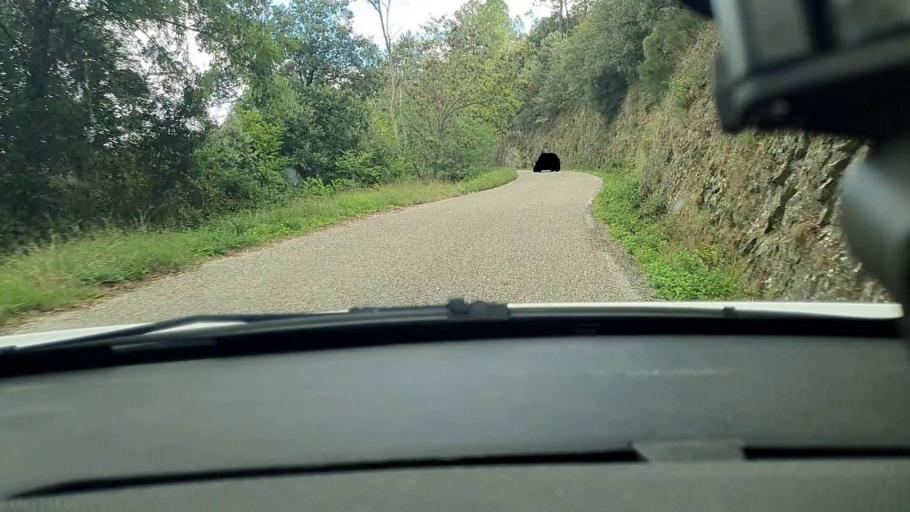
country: FR
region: Languedoc-Roussillon
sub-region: Departement du Gard
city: Branoux-les-Taillades
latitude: 44.2980
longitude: 3.9952
